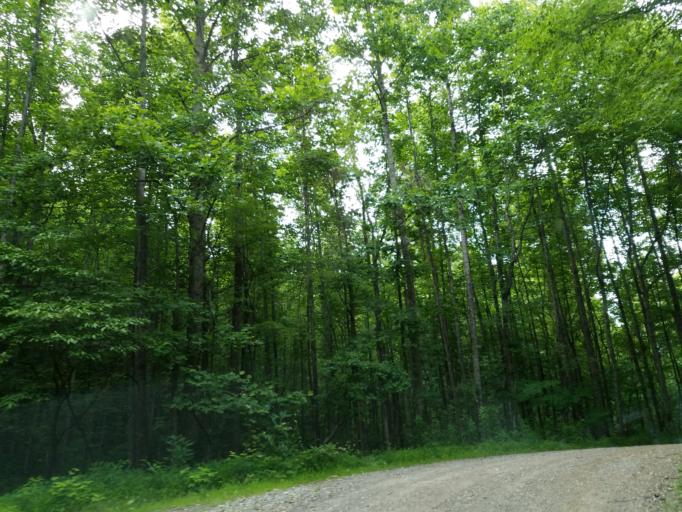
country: US
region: Georgia
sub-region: Union County
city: Blairsville
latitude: 34.7311
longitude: -84.0627
